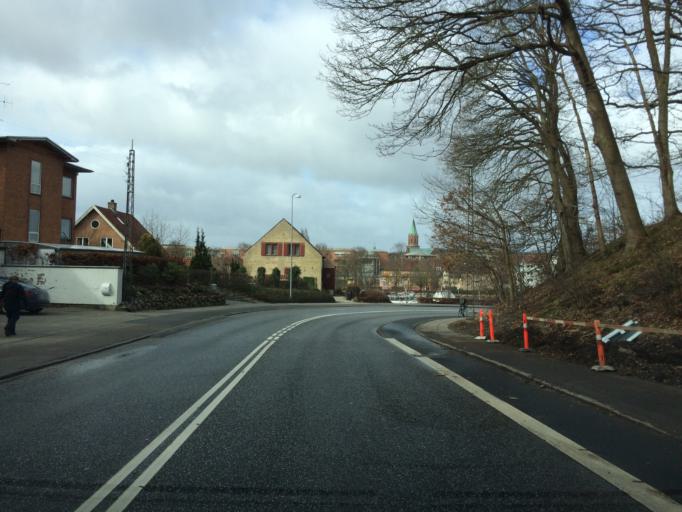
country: DK
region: Central Jutland
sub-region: Silkeborg Kommune
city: Silkeborg
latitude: 56.1694
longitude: 9.5576
